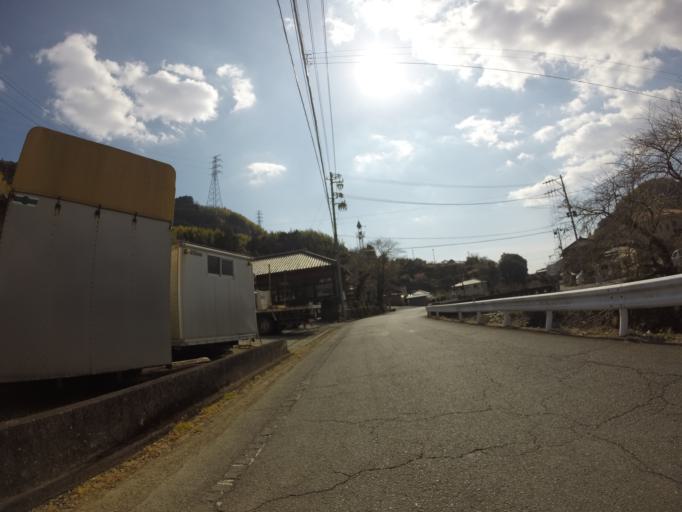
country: JP
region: Shizuoka
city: Shizuoka-shi
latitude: 35.0712
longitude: 138.4847
